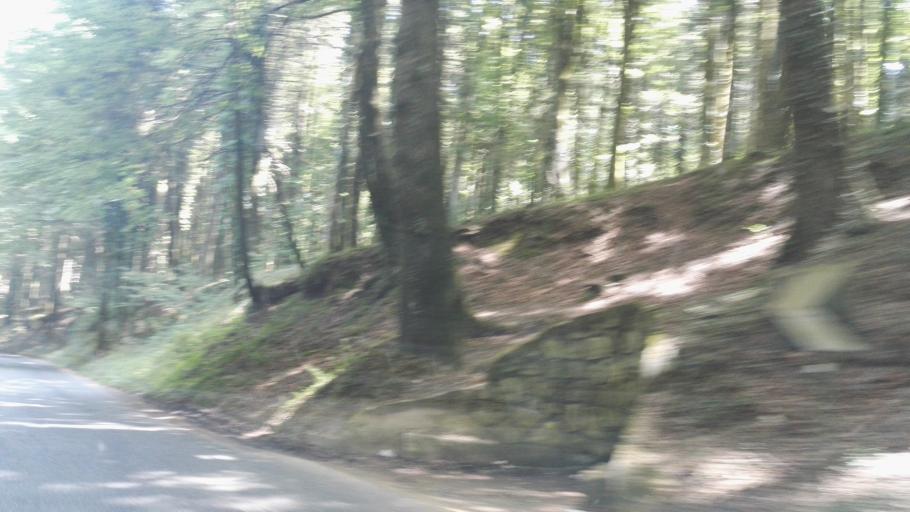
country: IT
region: Calabria
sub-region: Provincia di Vibo-Valentia
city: Mongiana
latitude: 38.5435
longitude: 16.3180
